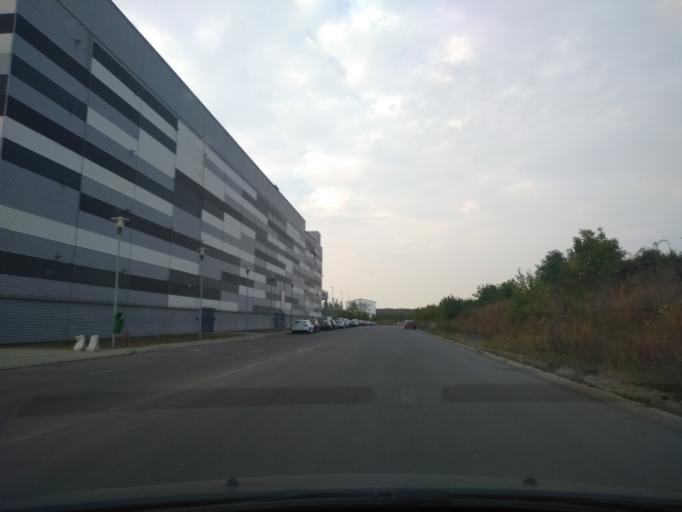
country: RO
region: Ilfov
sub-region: Comuna Otopeni
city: Otopeni
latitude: 44.5057
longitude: 26.0908
